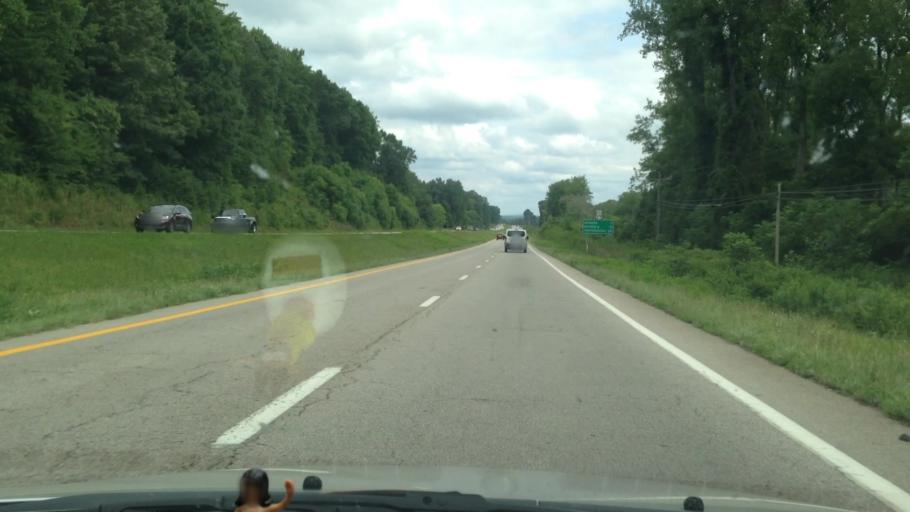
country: US
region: Virginia
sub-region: Pittsylvania County
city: Gretna
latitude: 36.9909
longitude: -79.3553
